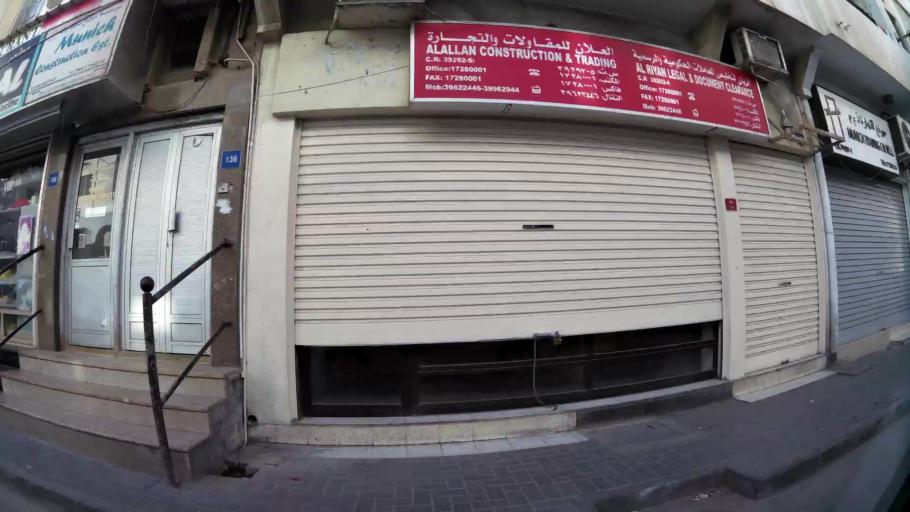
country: BH
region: Manama
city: Manama
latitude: 26.2323
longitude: 50.5875
